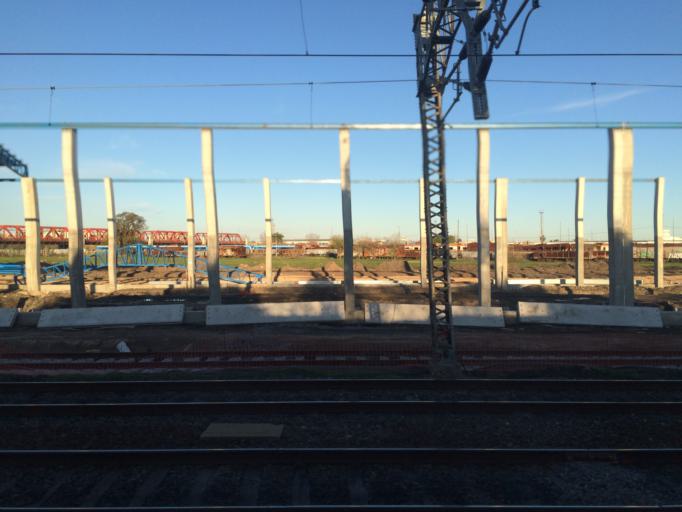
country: AR
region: Buenos Aires
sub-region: Partido de Avellaneda
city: Avellaneda
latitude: -34.6741
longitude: -58.3784
